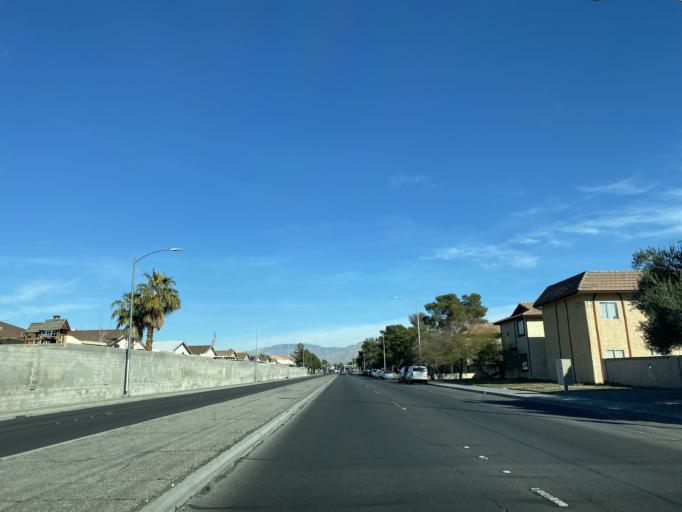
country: US
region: Nevada
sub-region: Clark County
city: Las Vegas
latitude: 36.1997
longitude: -115.2238
